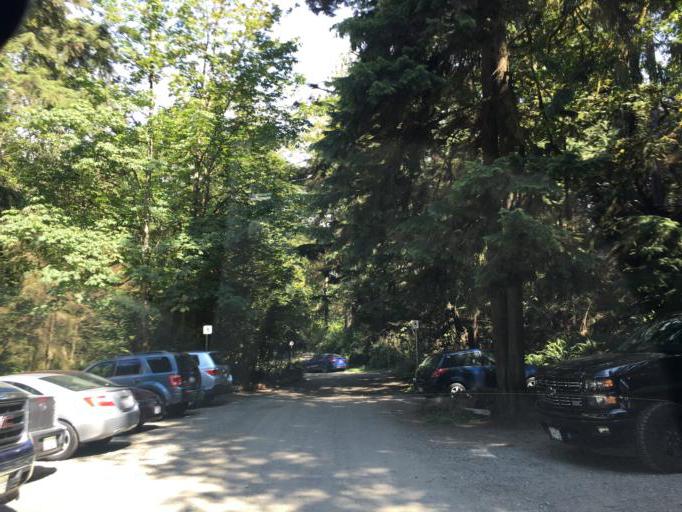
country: CA
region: British Columbia
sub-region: Greater Vancouver Regional District
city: Bowen Island
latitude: 49.3380
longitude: -123.2632
